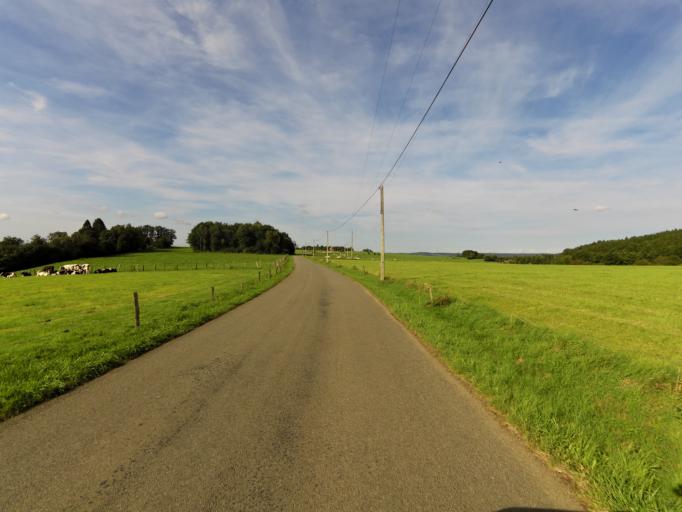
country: BE
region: Wallonia
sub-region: Province du Luxembourg
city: Rendeux
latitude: 50.2410
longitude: 5.5510
